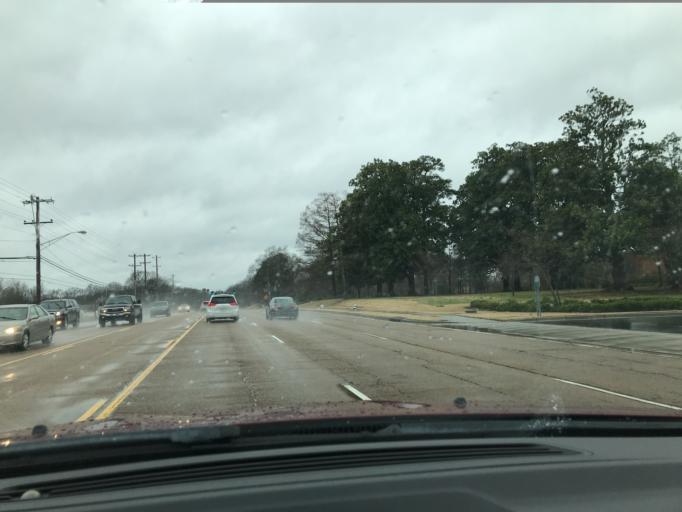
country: US
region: Tennessee
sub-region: Shelby County
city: Collierville
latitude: 35.0470
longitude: -89.7096
